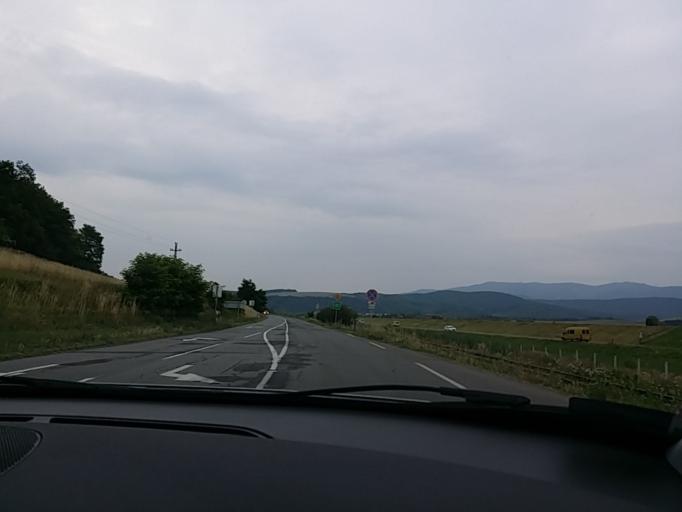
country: HU
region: Nograd
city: Batonyterenye
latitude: 47.9997
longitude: 19.8512
